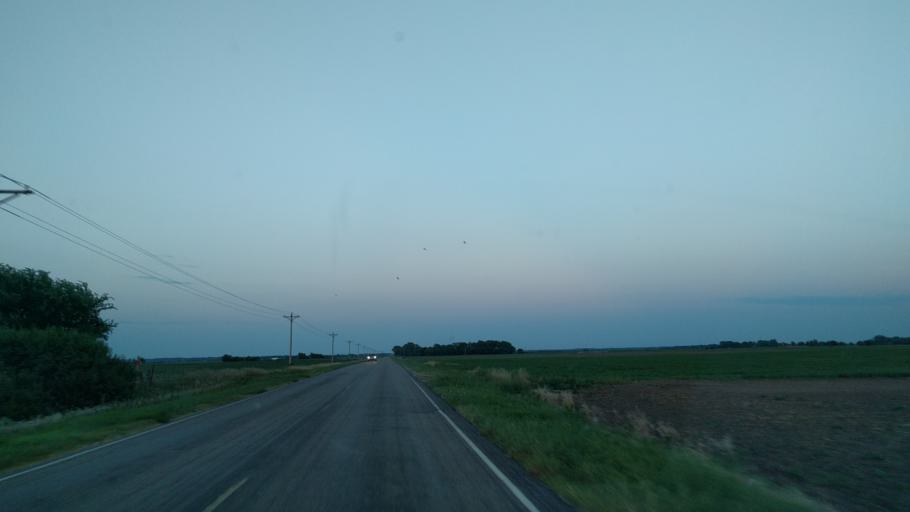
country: US
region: Kansas
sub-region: Reno County
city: Nickerson
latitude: 38.2177
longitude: -98.1163
